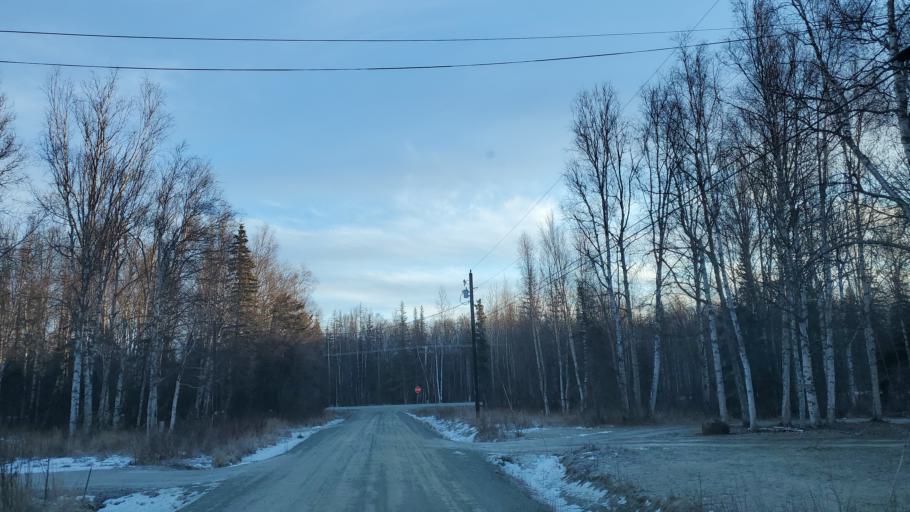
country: US
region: Alaska
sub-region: Matanuska-Susitna Borough
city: Lakes
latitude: 61.6518
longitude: -149.3157
